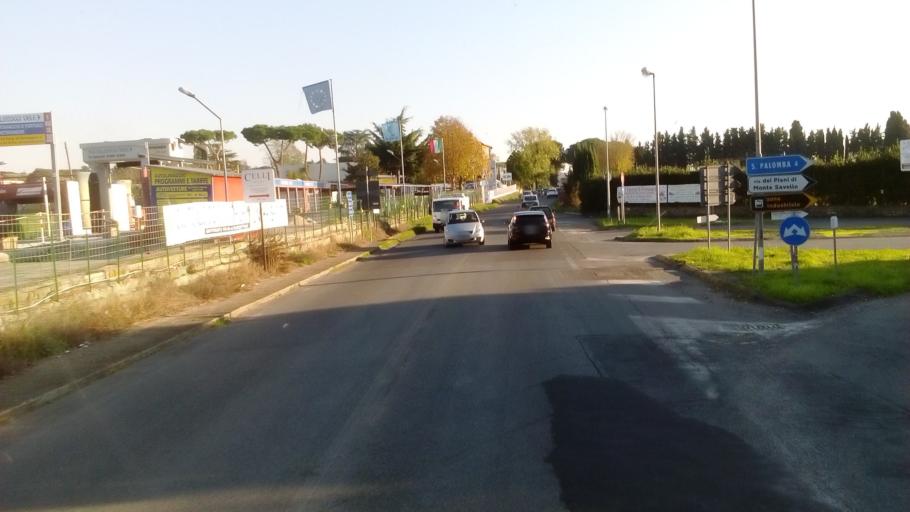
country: IT
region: Latium
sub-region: Citta metropolitana di Roma Capitale
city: Pavona
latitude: 41.7216
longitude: 12.6206
